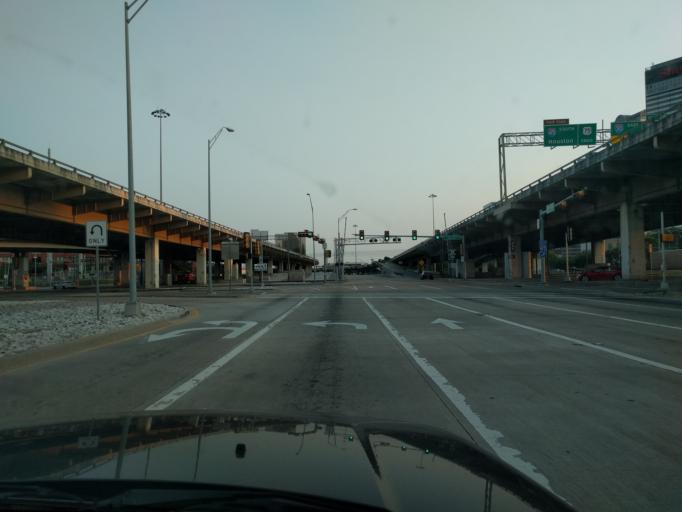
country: US
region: Texas
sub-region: Dallas County
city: Dallas
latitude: 32.7890
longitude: -96.7922
